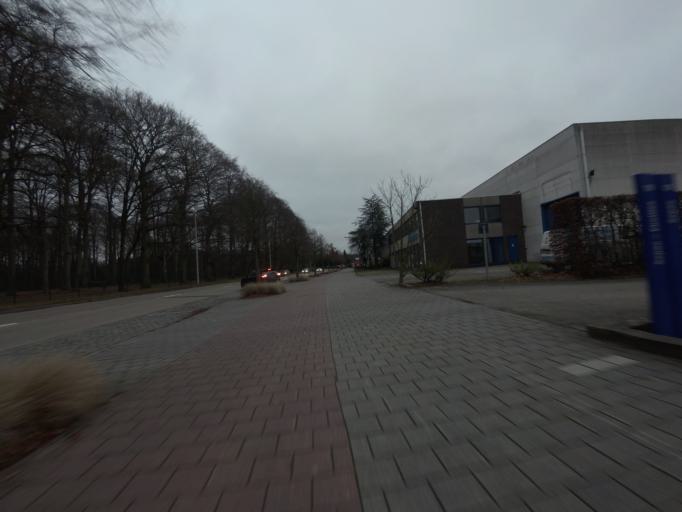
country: BE
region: Flanders
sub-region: Provincie Antwerpen
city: Hoboken
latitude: 51.1612
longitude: 4.3695
